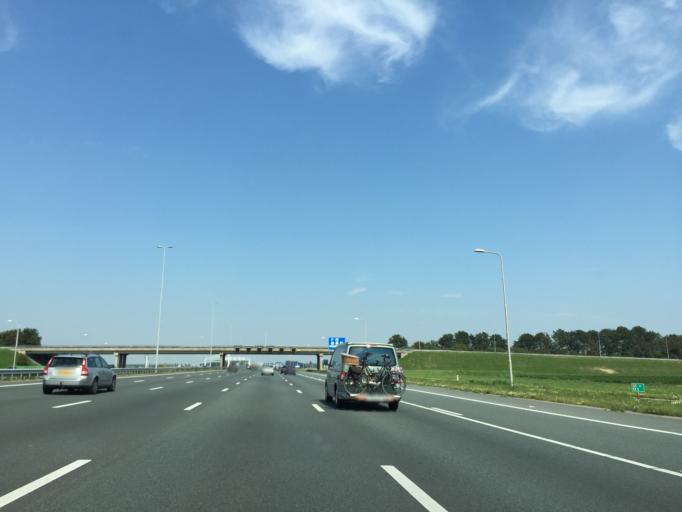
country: NL
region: South Holland
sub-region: Gemeente Kaag en Braassem
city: Leimuiden
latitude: 52.2453
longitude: 4.6656
